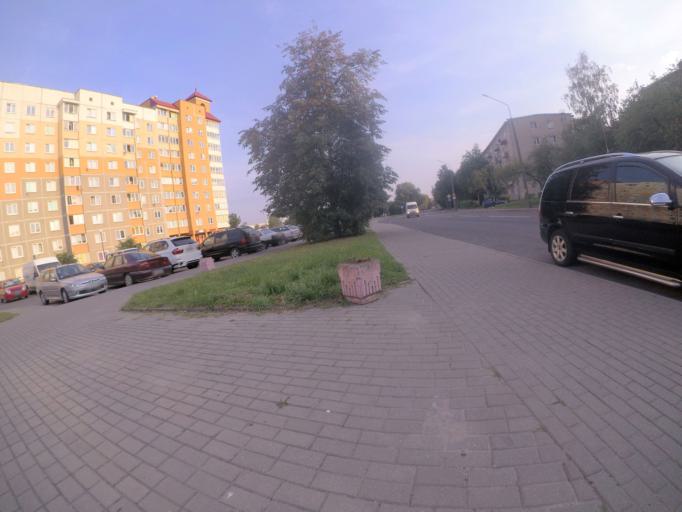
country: BY
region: Grodnenskaya
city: Hrodna
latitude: 53.6954
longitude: 23.8353
